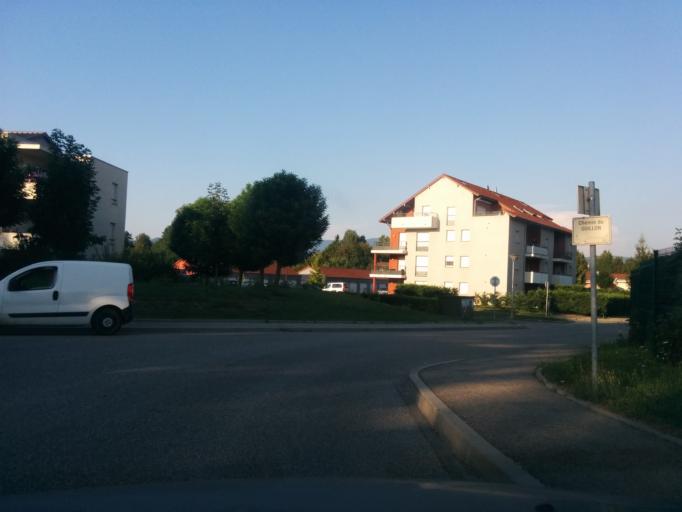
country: FR
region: Rhone-Alpes
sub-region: Departement de la Savoie
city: Le Pont-de-Beauvoisin
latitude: 45.5387
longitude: 5.6552
